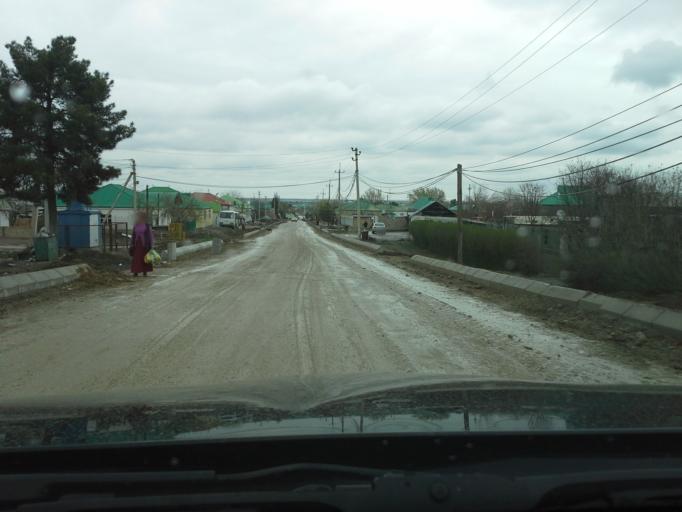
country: TM
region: Ahal
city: Abadan
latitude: 37.9632
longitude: 58.2126
